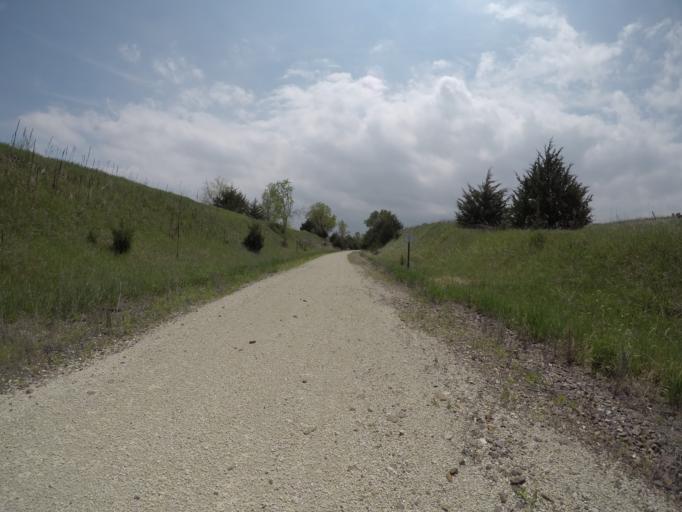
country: US
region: Nebraska
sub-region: Gage County
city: Wymore
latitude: 40.2101
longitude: -96.6611
